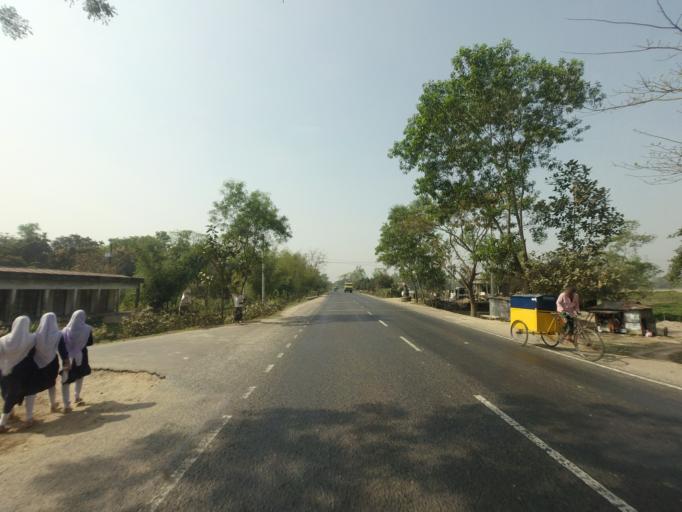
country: BD
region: Sylhet
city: Habiganj
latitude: 24.3989
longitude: 91.5630
